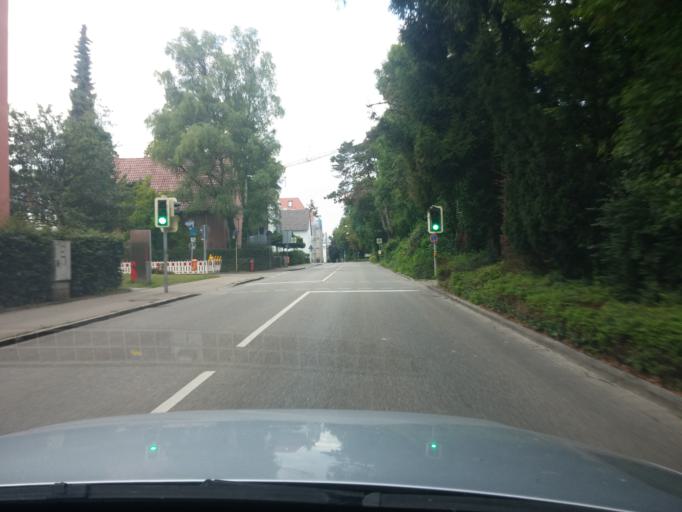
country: DE
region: Bavaria
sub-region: Swabia
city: Memmingen
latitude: 47.9806
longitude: 10.1792
